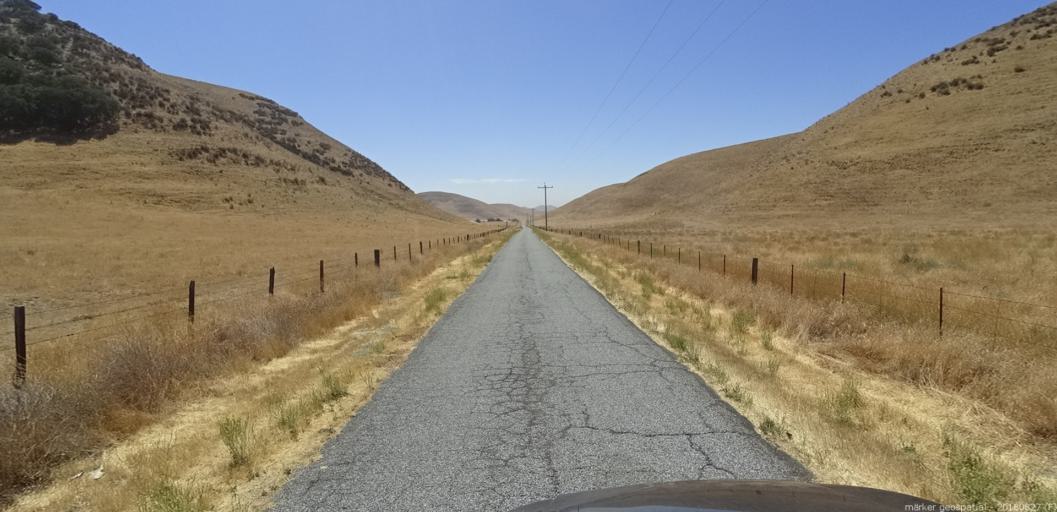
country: US
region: California
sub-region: Monterey County
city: King City
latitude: 36.1490
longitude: -120.8675
